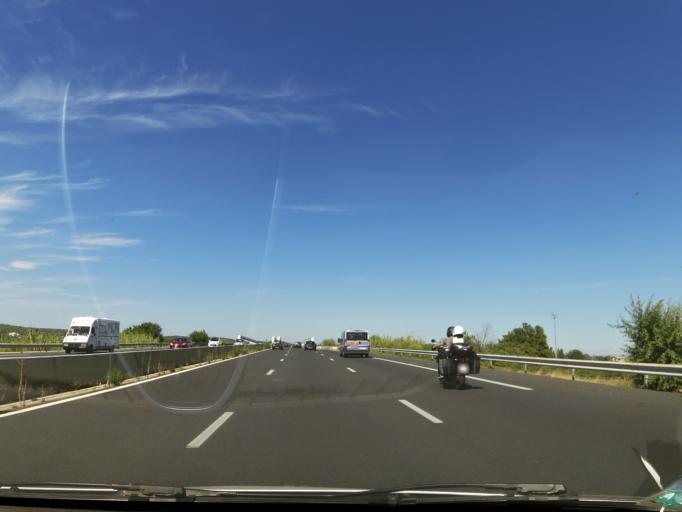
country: FR
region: Languedoc-Roussillon
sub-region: Departement du Gard
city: Rodilhan
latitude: 43.8420
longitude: 4.4151
